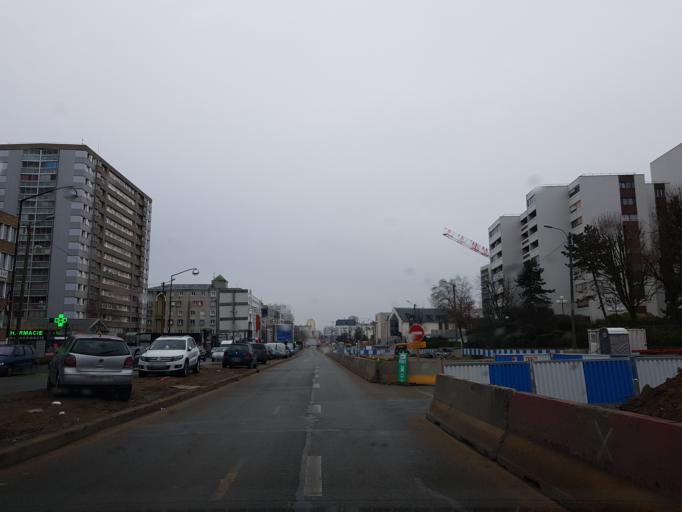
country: FR
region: Ile-de-France
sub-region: Departement du Val-de-Marne
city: Vitry-sur-Seine
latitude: 48.7915
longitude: 2.3874
